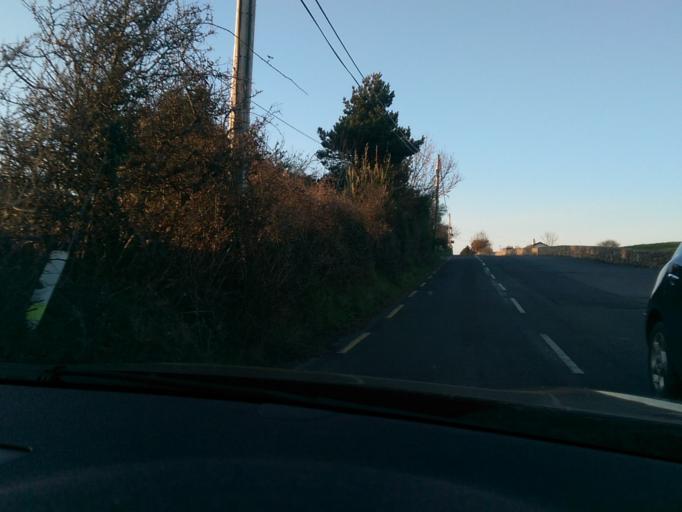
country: IE
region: Connaught
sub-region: County Galway
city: Gaillimh
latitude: 53.2796
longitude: -9.0834
